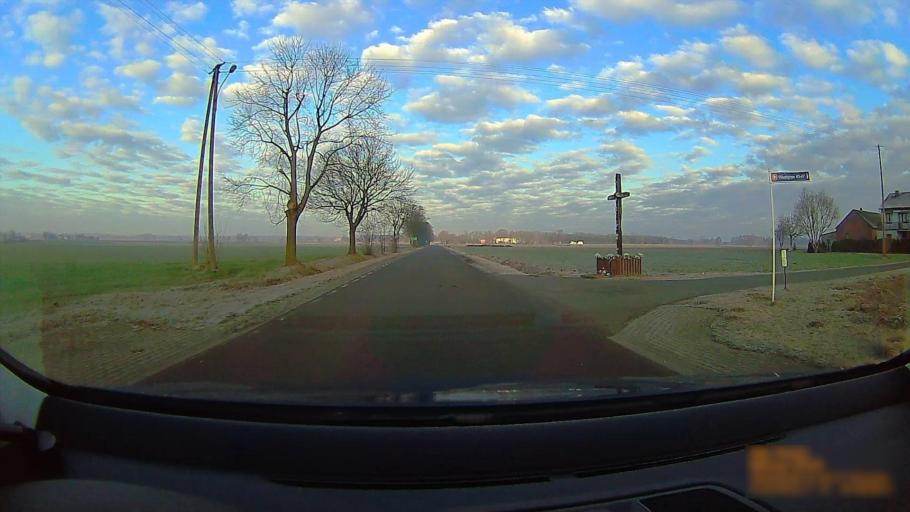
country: PL
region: Greater Poland Voivodeship
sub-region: Powiat koninski
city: Rychwal
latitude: 52.0981
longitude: 18.1105
